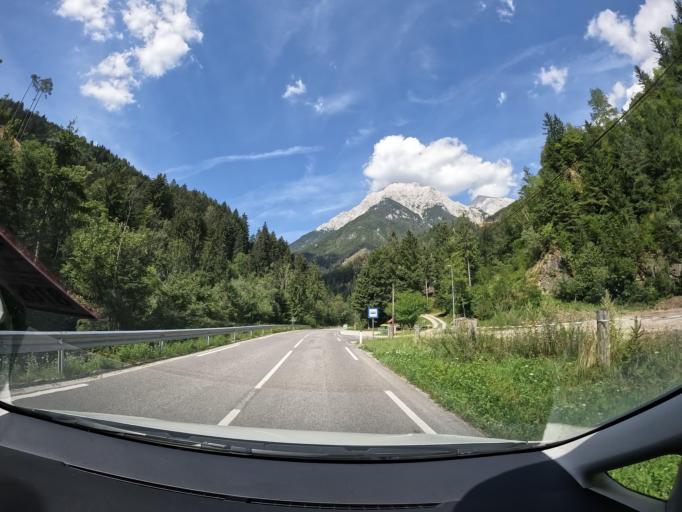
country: SI
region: Jezersko
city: Zgornje Jezersko
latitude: 46.3285
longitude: 14.4909
